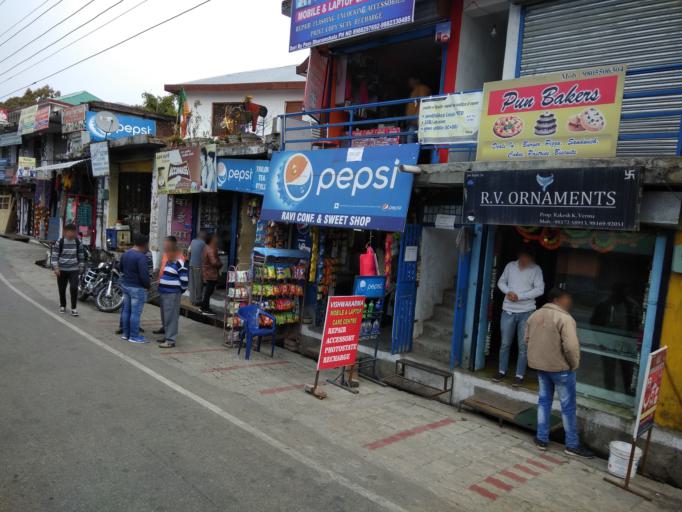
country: IN
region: Himachal Pradesh
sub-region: Kangra
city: Dharmsala
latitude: 32.2002
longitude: 76.3358
